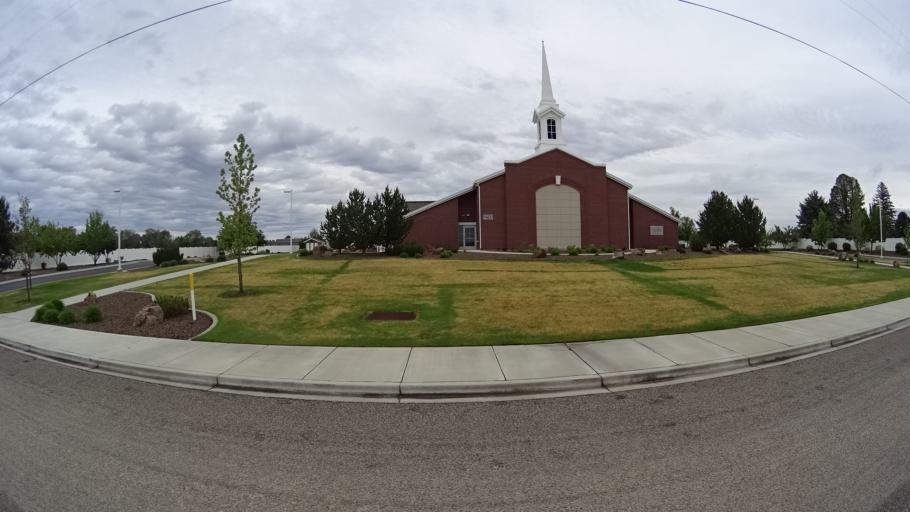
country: US
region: Idaho
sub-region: Ada County
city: Star
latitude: 43.7064
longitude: -116.4709
